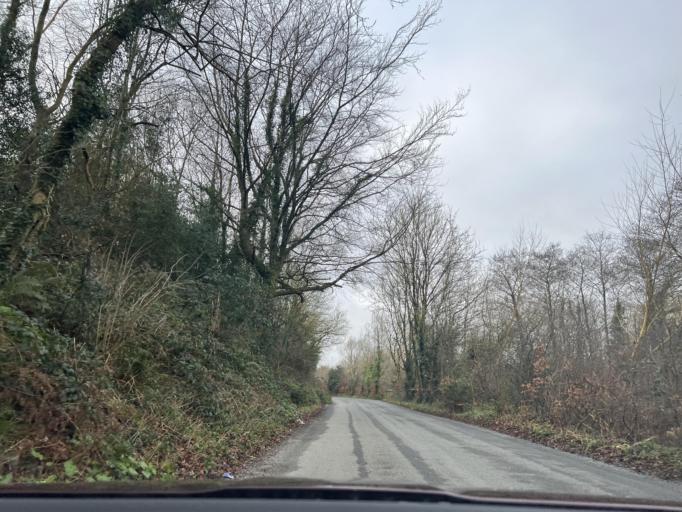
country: IE
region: Leinster
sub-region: Loch Garman
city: Enniscorthy
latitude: 52.3852
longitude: -6.5717
